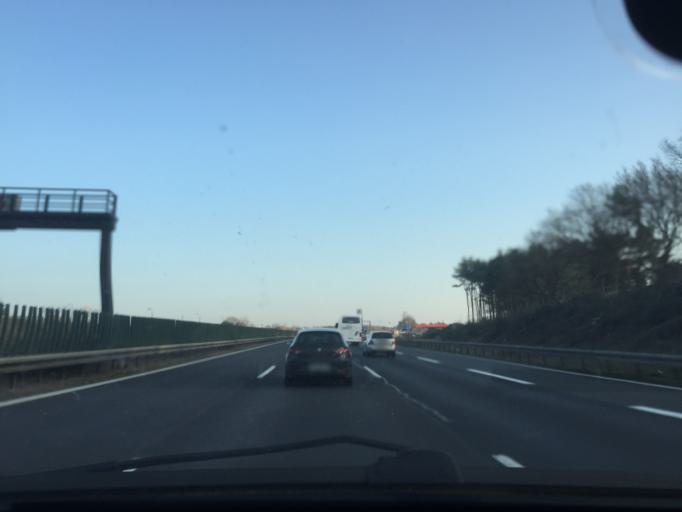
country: DE
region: Brandenburg
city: Michendorf
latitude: 52.3034
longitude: 13.0091
